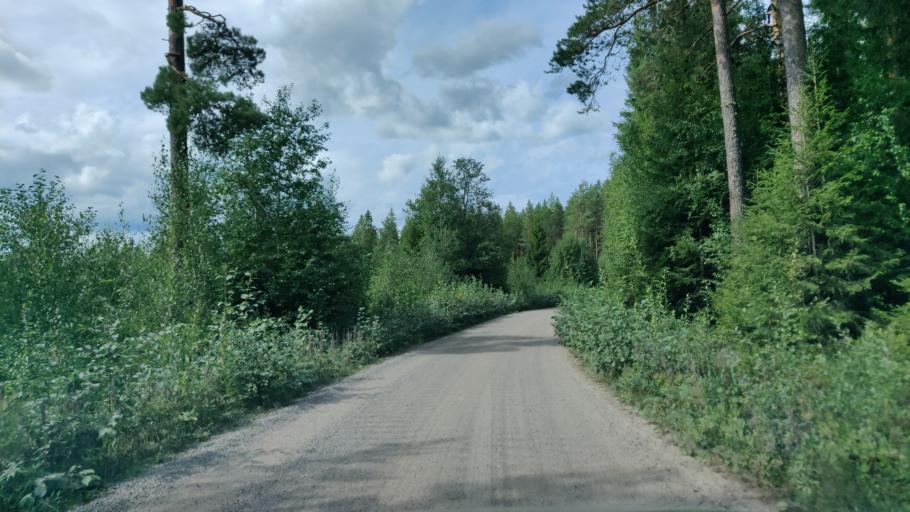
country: SE
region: Vaermland
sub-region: Hagfors Kommun
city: Hagfors
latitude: 60.0103
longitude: 13.7077
